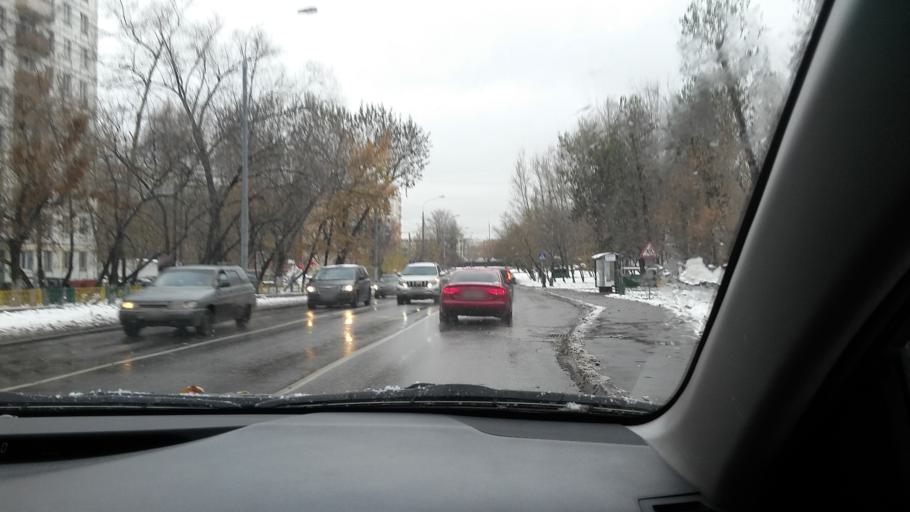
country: RU
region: Moscow
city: Novyye Kuz'minki
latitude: 55.7107
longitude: 37.7627
